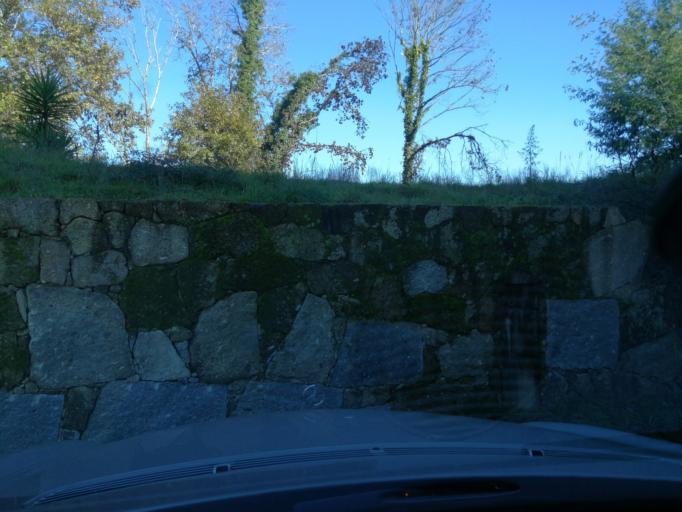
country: PT
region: Braga
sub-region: Braga
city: Adaufe
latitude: 41.6117
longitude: -8.3931
